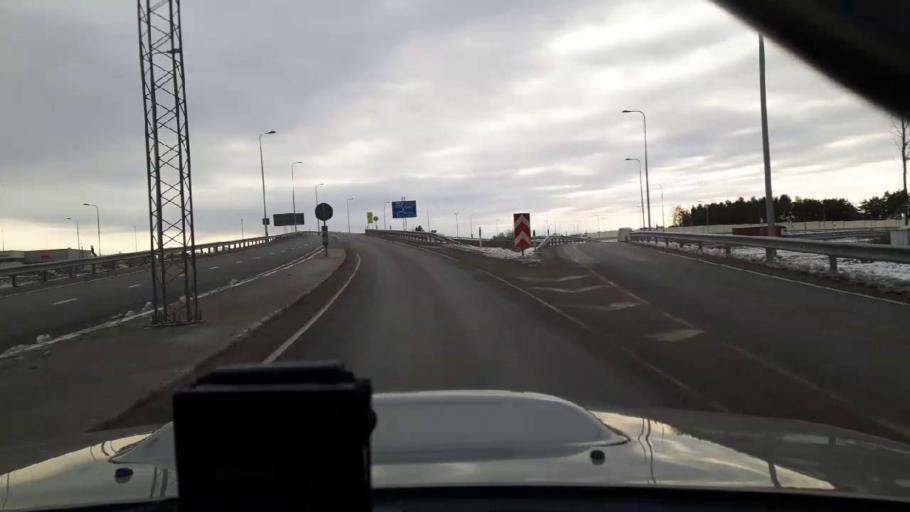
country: EE
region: Harju
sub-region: Saue vald
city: Laagri
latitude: 59.3397
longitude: 24.6097
